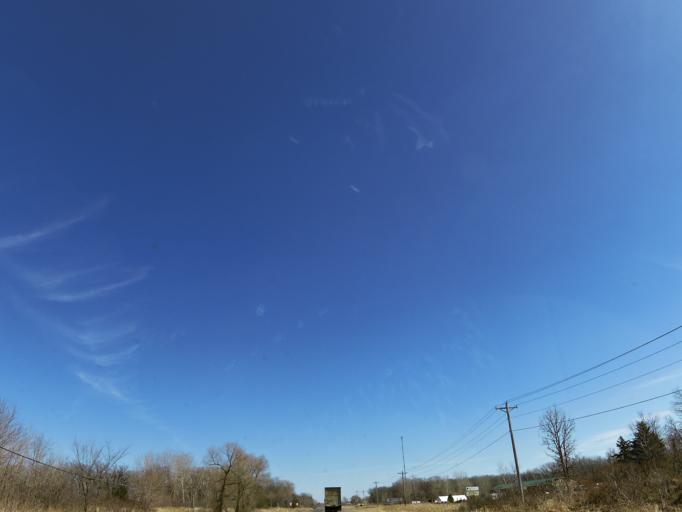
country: US
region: Minnesota
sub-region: Hennepin County
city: Medina
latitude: 45.0564
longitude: -93.5830
